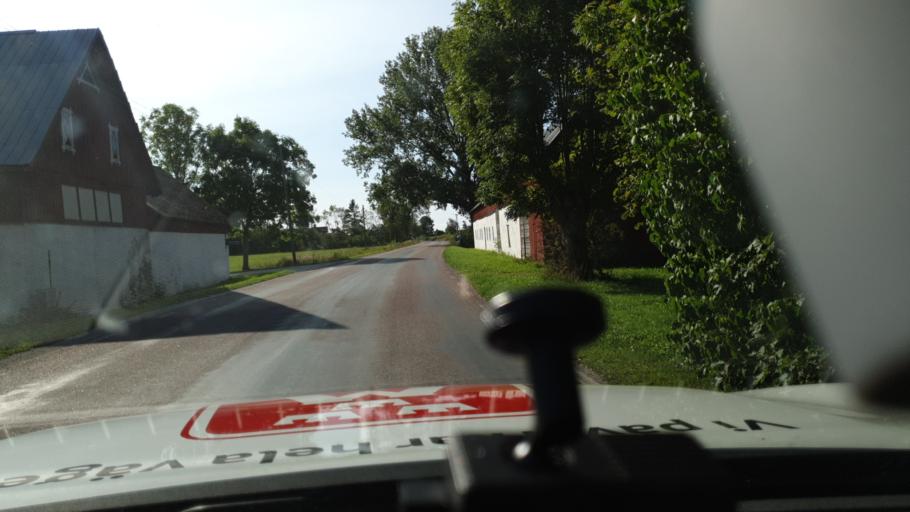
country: SE
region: Gotland
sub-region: Gotland
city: Hemse
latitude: 57.1598
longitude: 18.2812
